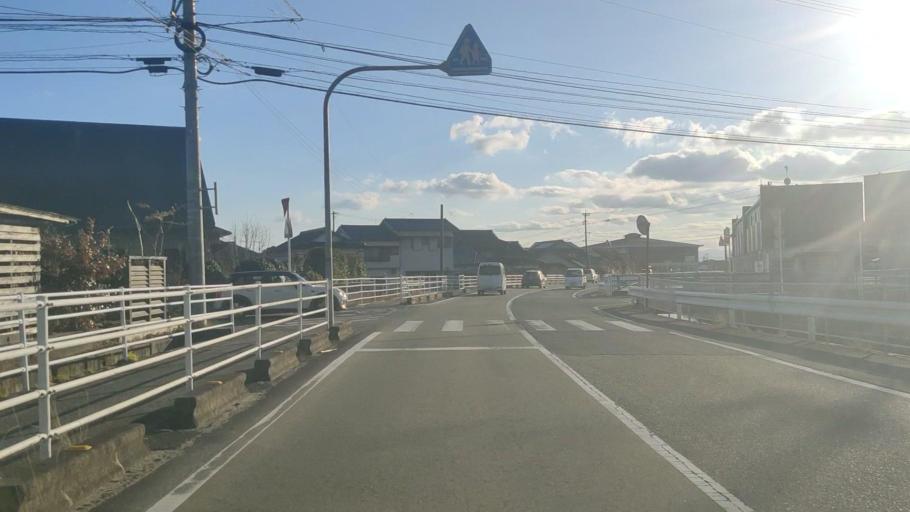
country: JP
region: Saga Prefecture
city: Saga-shi
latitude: 33.2767
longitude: 130.2228
